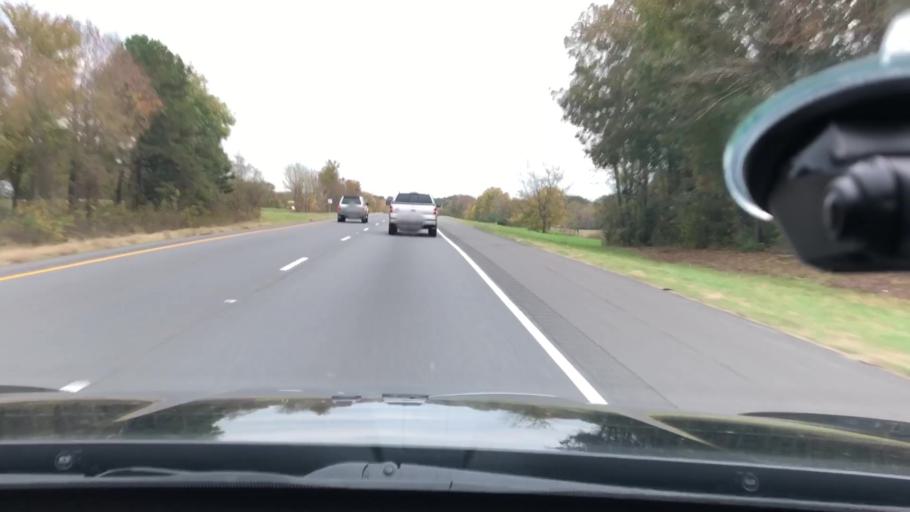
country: US
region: Arkansas
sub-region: Hempstead County
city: Hope
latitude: 33.7205
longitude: -93.5556
